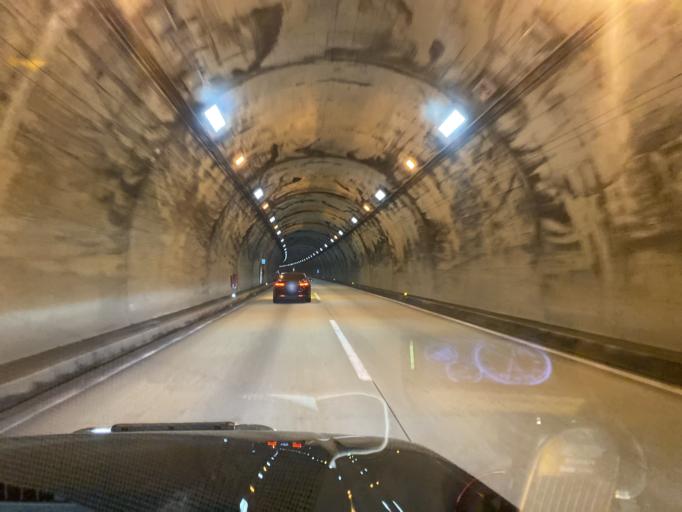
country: JP
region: Hyogo
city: Sasayama
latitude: 35.0295
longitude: 135.1793
